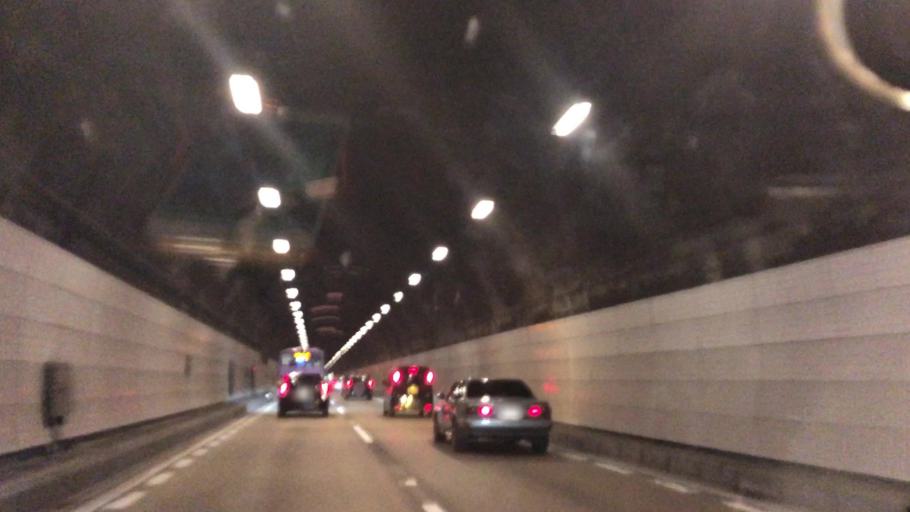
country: JP
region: Miyagi
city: Sendai
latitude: 38.2617
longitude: 140.8384
